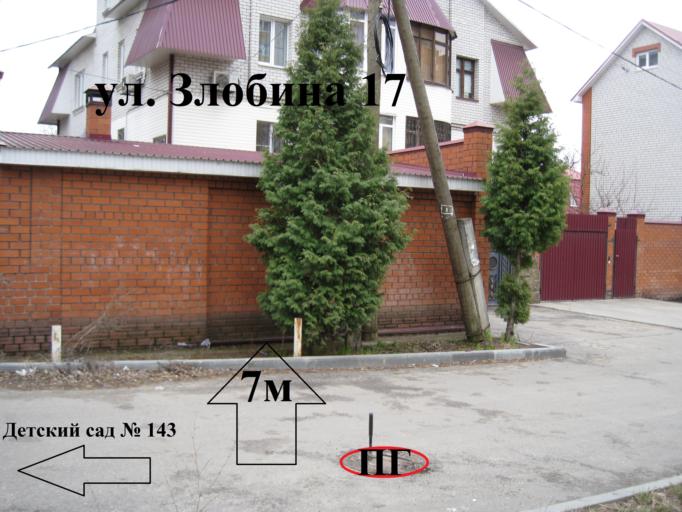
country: RU
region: Voronezj
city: Voronezh
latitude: 51.6505
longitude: 39.1815
